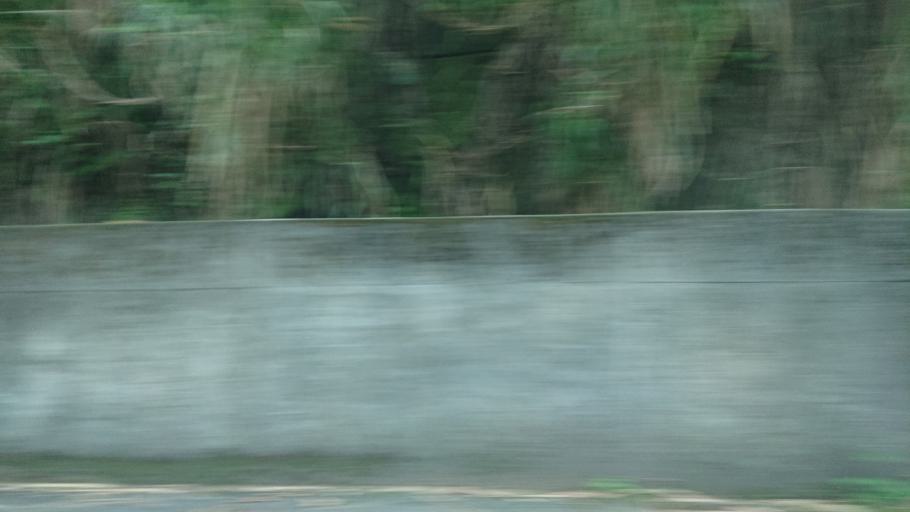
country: TW
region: Taiwan
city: Daxi
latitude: 24.8796
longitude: 121.3812
